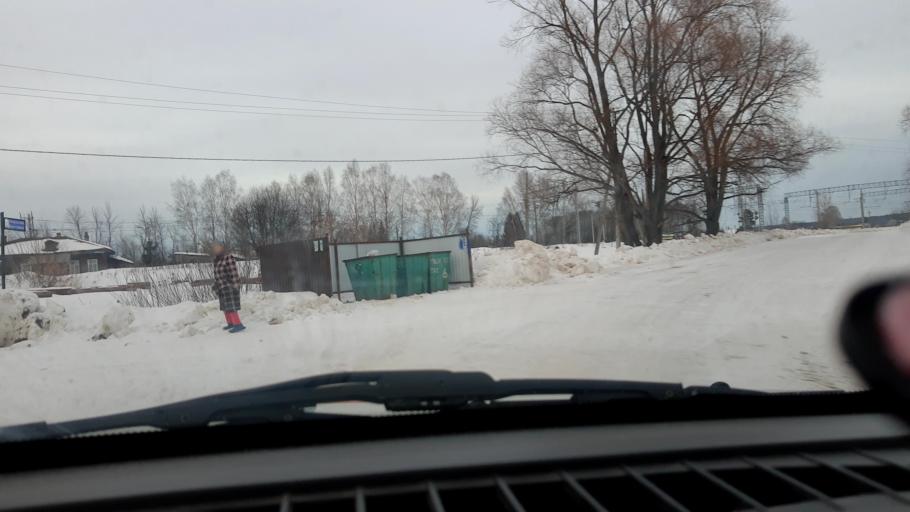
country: RU
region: Bashkortostan
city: Urman
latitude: 54.8742
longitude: 56.8695
